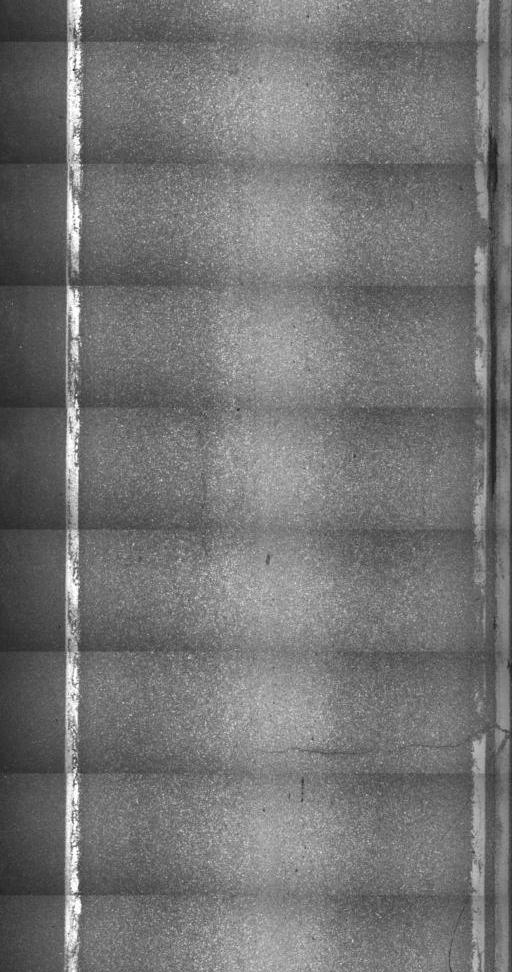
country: US
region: Vermont
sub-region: Orleans County
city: Newport
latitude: 44.9325
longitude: -72.2422
